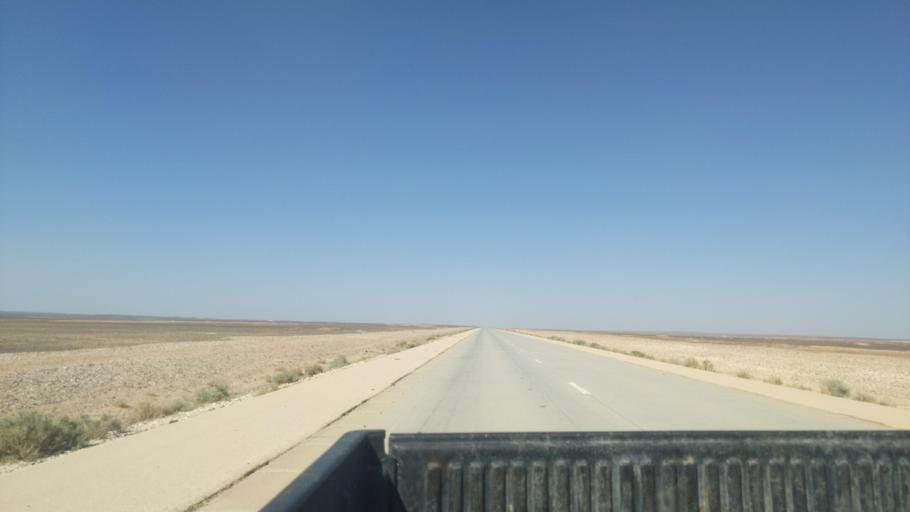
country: JO
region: Amman
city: Al Azraq ash Shamali
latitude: 31.4553
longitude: 36.7826
